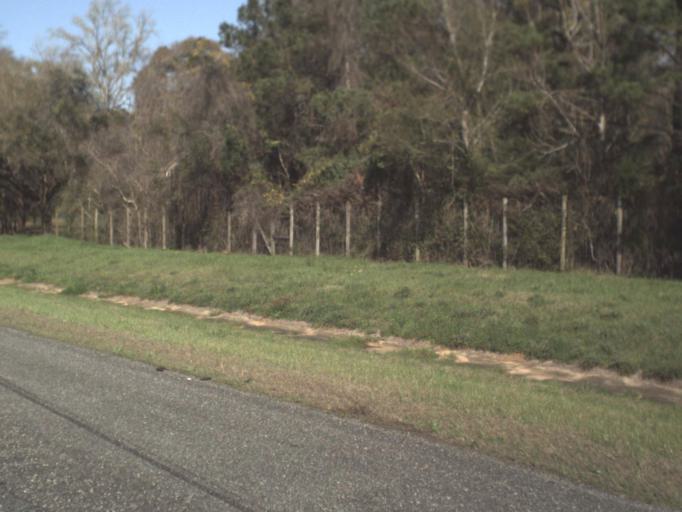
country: US
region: Florida
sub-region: Leon County
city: Tallahassee
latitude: 30.4784
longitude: -84.1359
